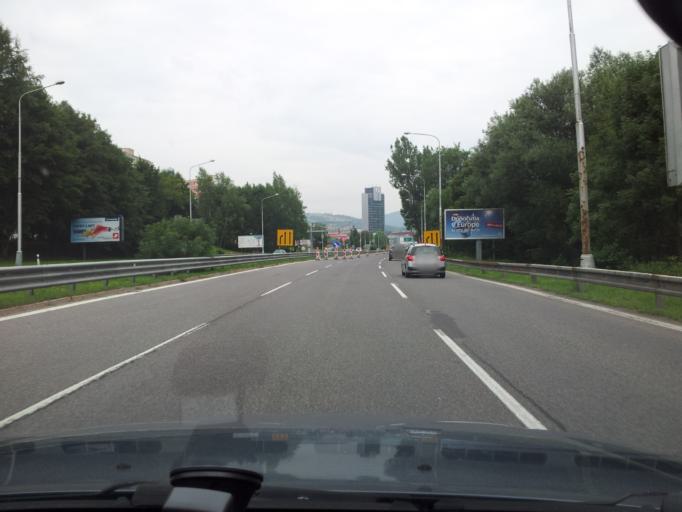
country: SK
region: Banskobystricky
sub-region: Okres Banska Bystrica
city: Banska Bystrica
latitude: 48.7218
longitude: 19.1376
